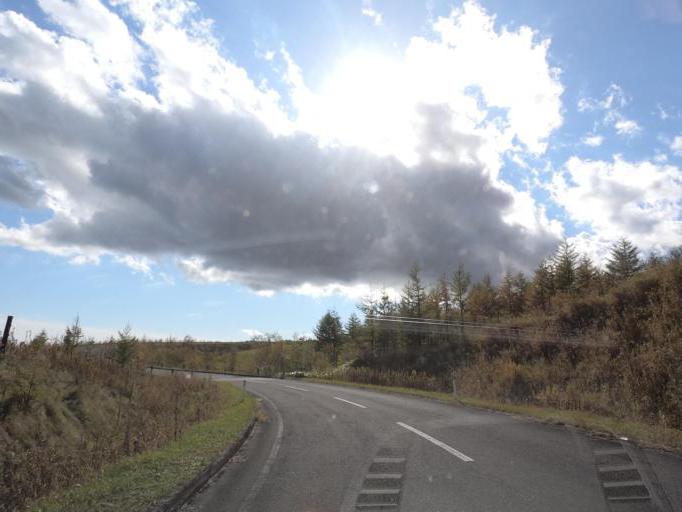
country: JP
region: Hokkaido
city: Otofuke
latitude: 43.2930
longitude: 143.1910
